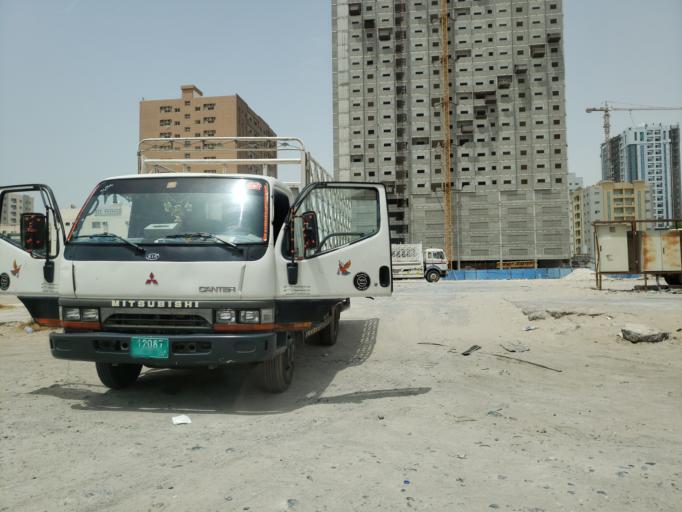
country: AE
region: Ajman
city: Ajman
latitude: 25.3915
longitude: 55.4630
